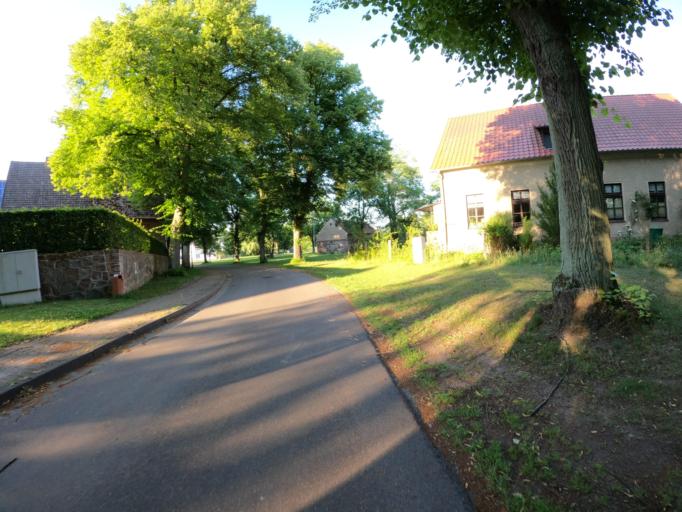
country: DE
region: Brandenburg
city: Tantow
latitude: 53.3043
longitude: 14.3859
